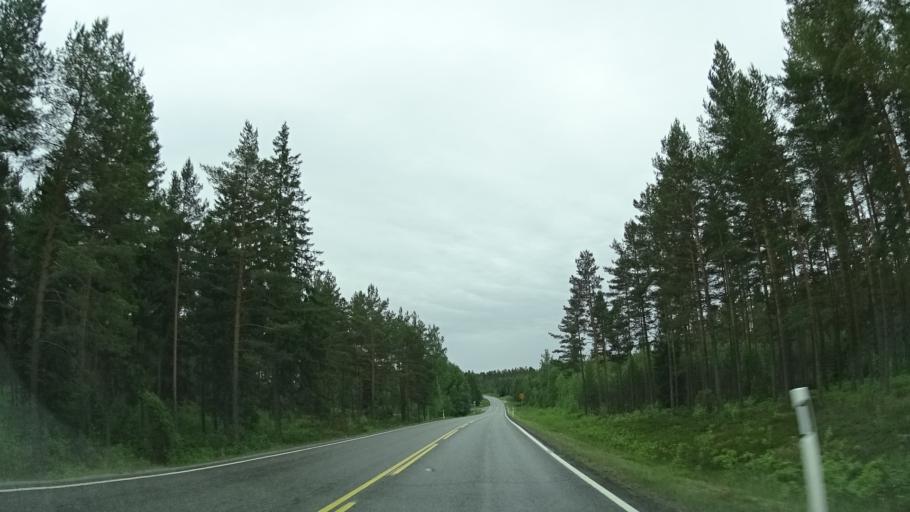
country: FI
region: Varsinais-Suomi
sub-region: Salo
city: Pernioe
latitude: 60.1012
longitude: 23.2183
